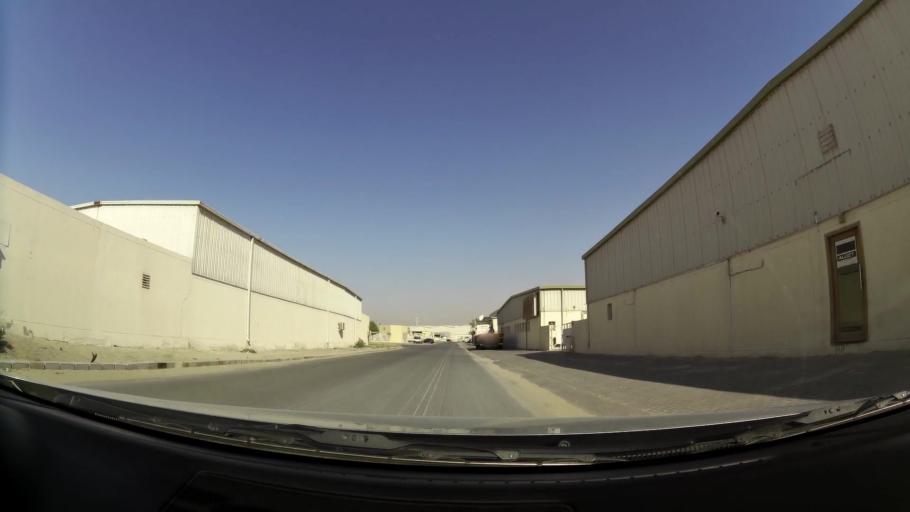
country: AE
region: Dubai
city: Dubai
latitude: 24.9874
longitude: 55.1127
